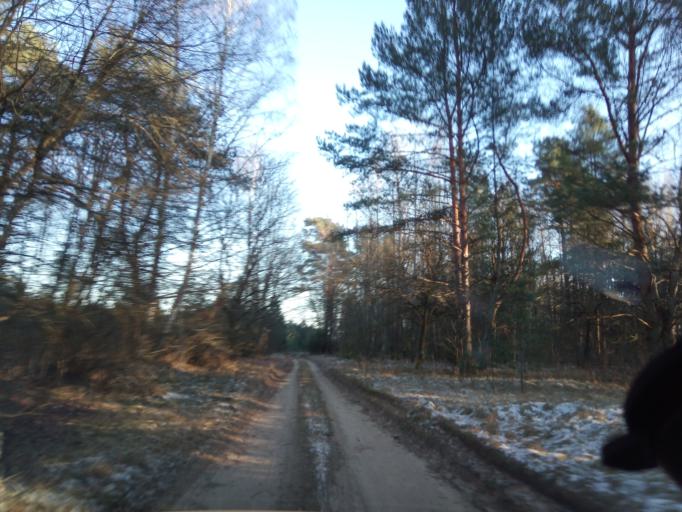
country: LT
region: Alytaus apskritis
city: Druskininkai
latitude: 53.9734
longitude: 23.9519
